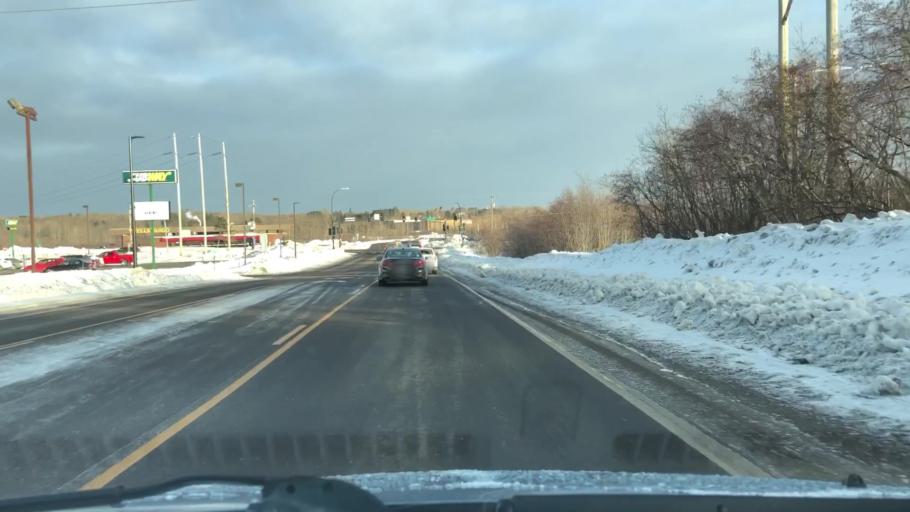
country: US
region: Minnesota
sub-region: Saint Louis County
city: Hermantown
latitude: 46.8130
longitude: -92.1770
